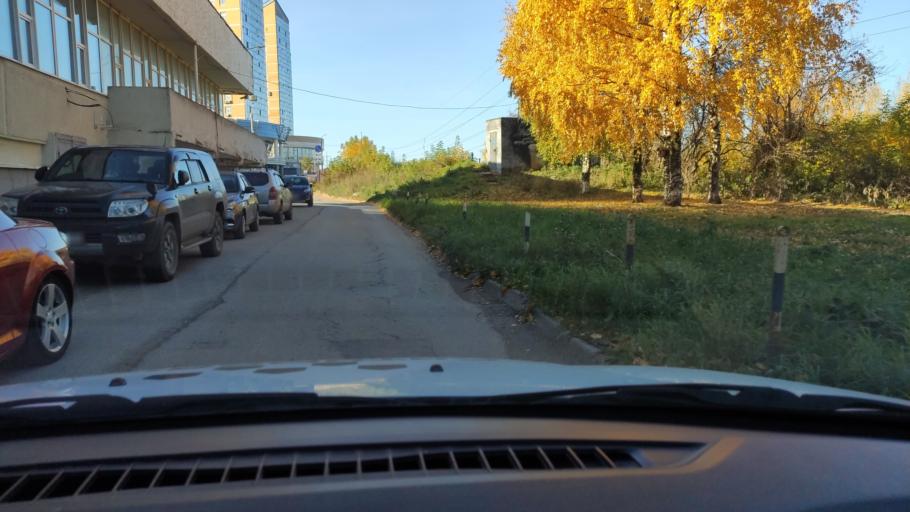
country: RU
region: Perm
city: Perm
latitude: 58.0235
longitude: 56.2705
